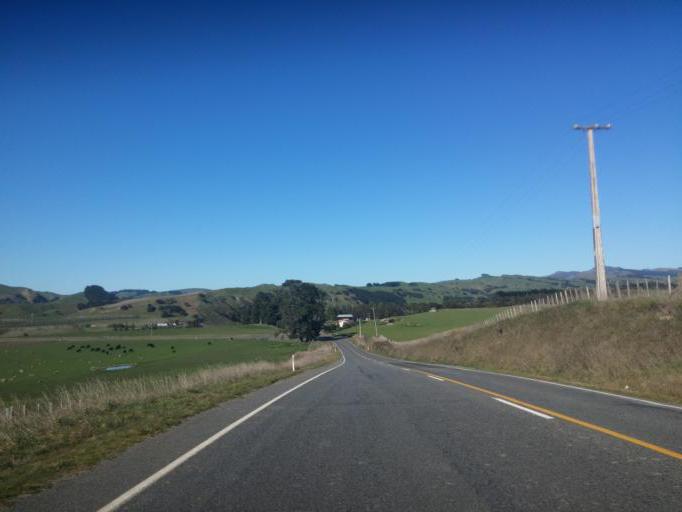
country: NZ
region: Wellington
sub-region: South Wairarapa District
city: Waipawa
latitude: -41.2928
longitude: 175.4623
